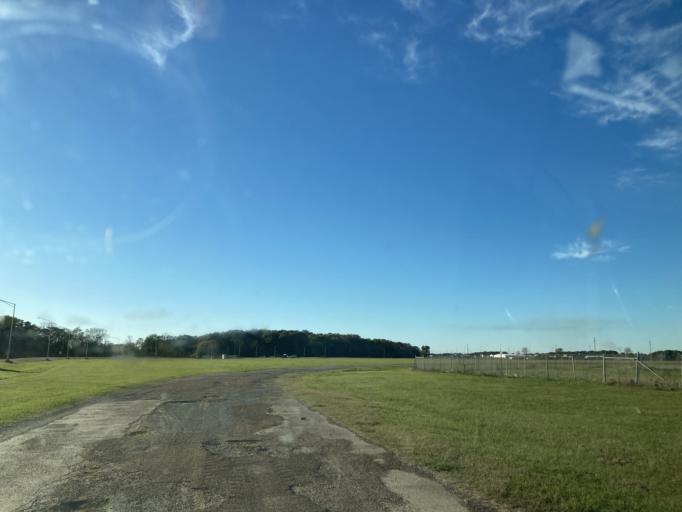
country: US
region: Mississippi
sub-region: Yazoo County
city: Yazoo City
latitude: 32.8797
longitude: -90.4191
